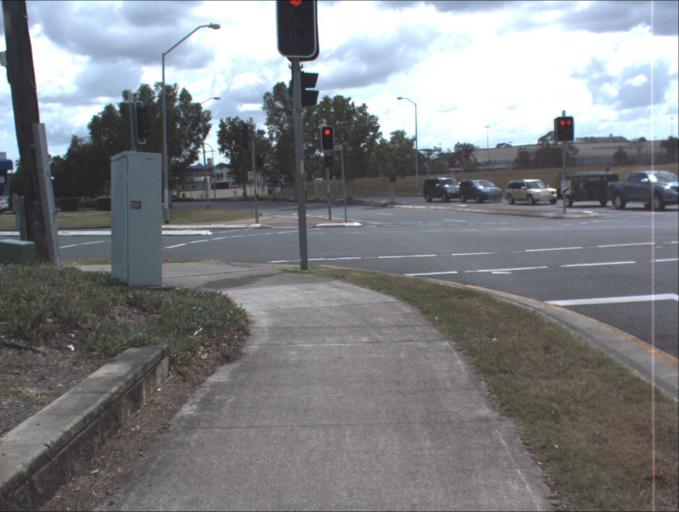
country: AU
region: Queensland
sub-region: Logan
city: Beenleigh
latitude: -27.7197
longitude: 153.2039
